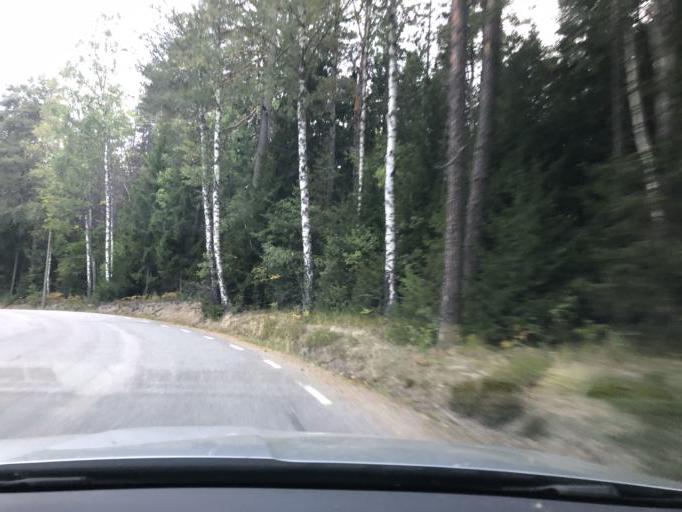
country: SE
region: Stockholm
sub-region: Botkyrka Kommun
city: Tullinge
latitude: 59.1092
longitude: 17.9772
